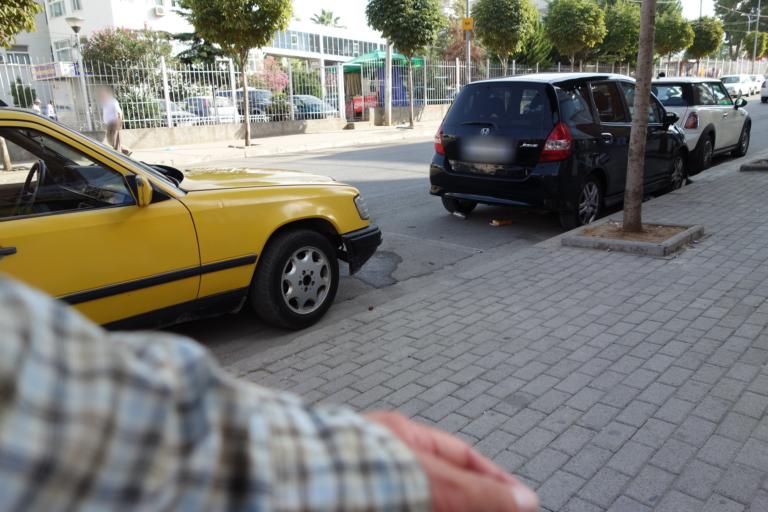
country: AL
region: Tirane
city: Tirana
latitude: 41.3388
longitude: 19.8353
